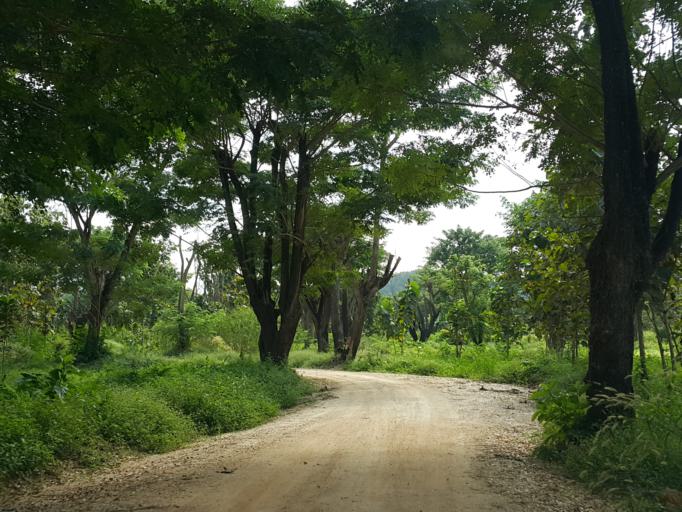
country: TH
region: Lampang
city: Hang Chat
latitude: 18.4828
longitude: 99.4028
